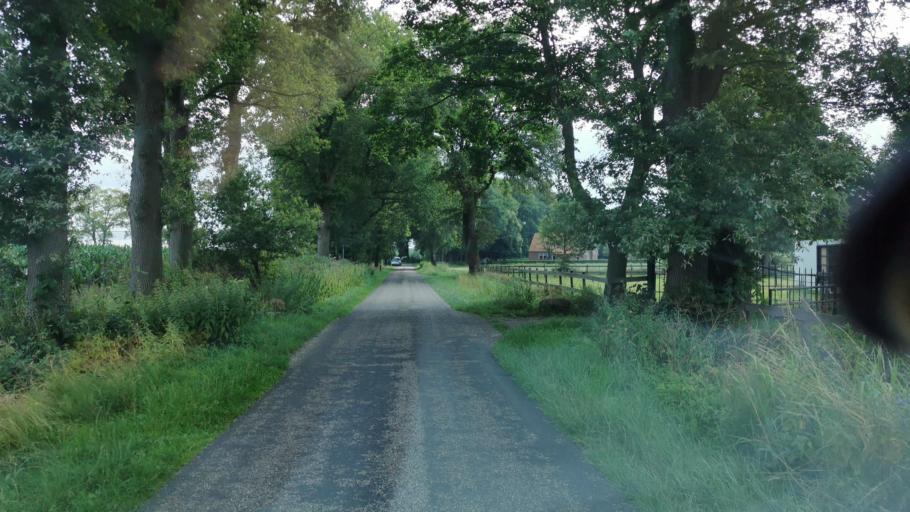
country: NL
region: Overijssel
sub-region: Gemeente Losser
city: Losser
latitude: 52.2434
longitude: 6.9960
